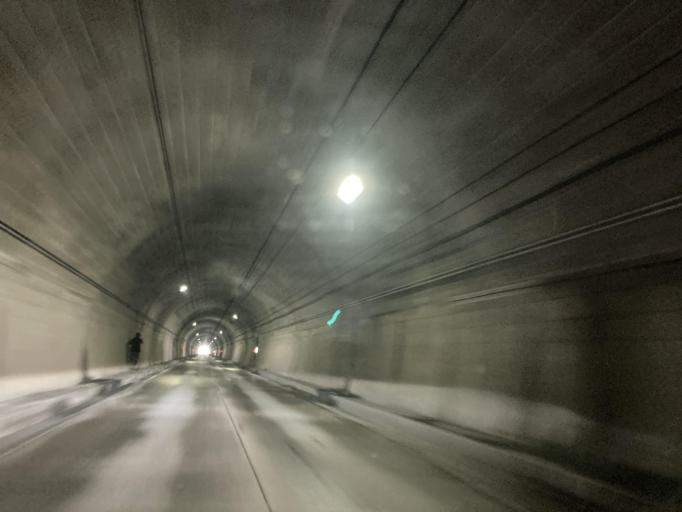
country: JP
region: Nagano
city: Omachi
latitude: 36.5093
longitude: 137.7637
